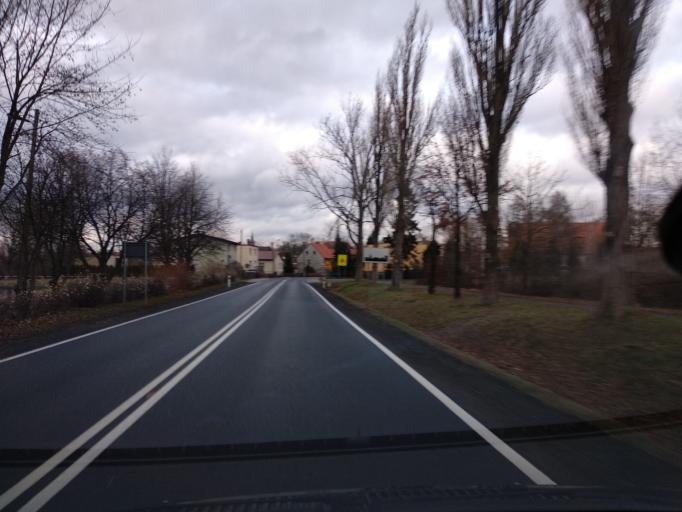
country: PL
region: Lower Silesian Voivodeship
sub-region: Powiat olesnicki
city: Miedzyborz
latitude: 51.3932
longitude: 17.6639
